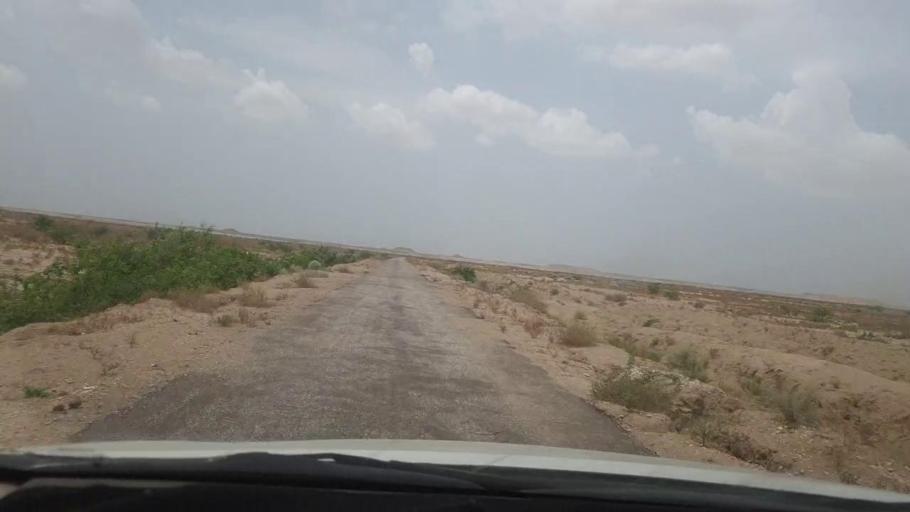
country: PK
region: Sindh
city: Khairpur
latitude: 27.4009
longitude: 68.9694
